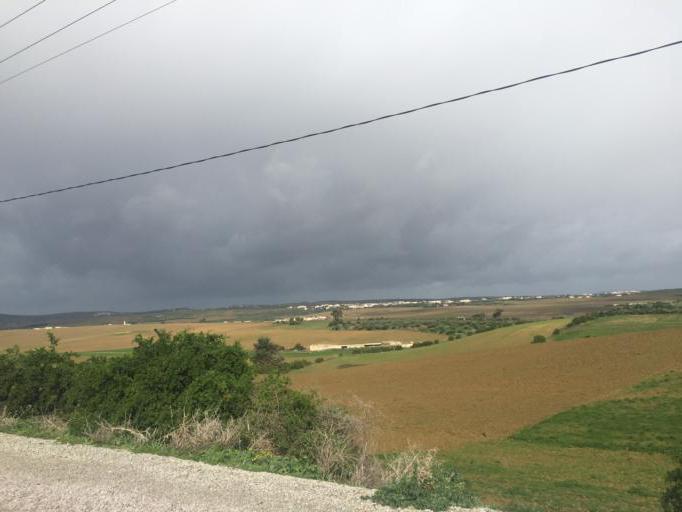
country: TN
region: Nabul
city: Menzel Heurr
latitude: 36.8350
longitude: 10.9588
